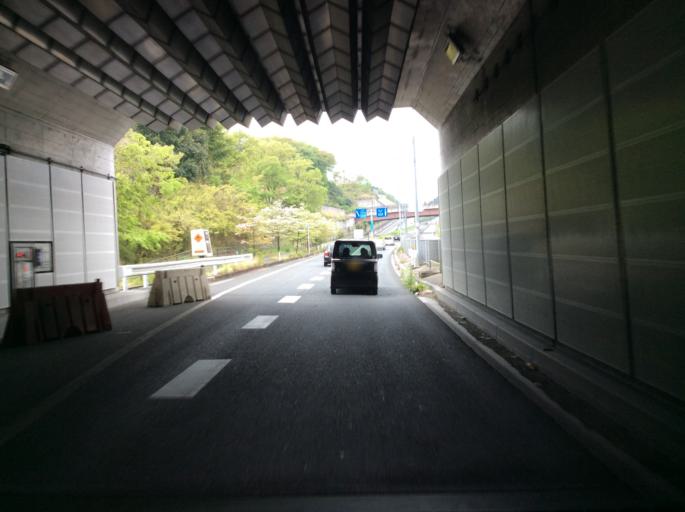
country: JP
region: Fukushima
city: Iwaki
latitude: 37.0316
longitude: 140.9101
